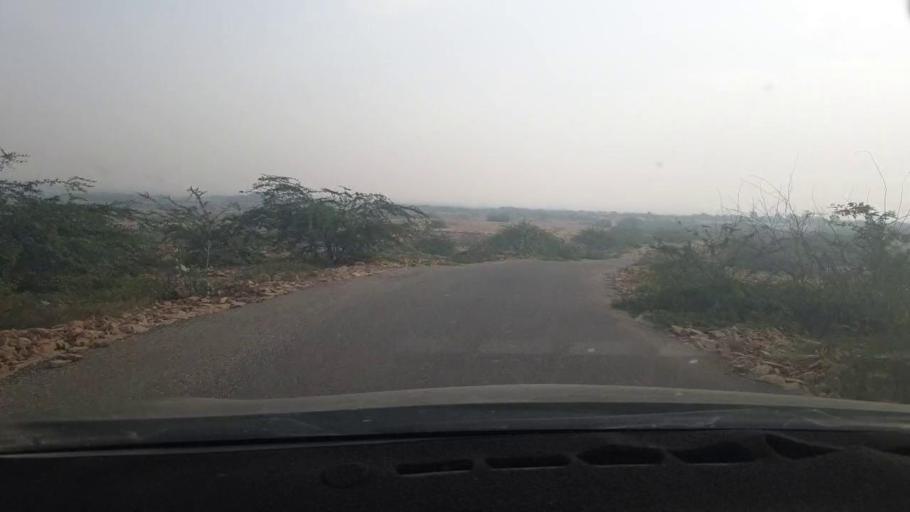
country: PK
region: Sindh
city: Malir Cantonment
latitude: 24.9517
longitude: 67.4340
